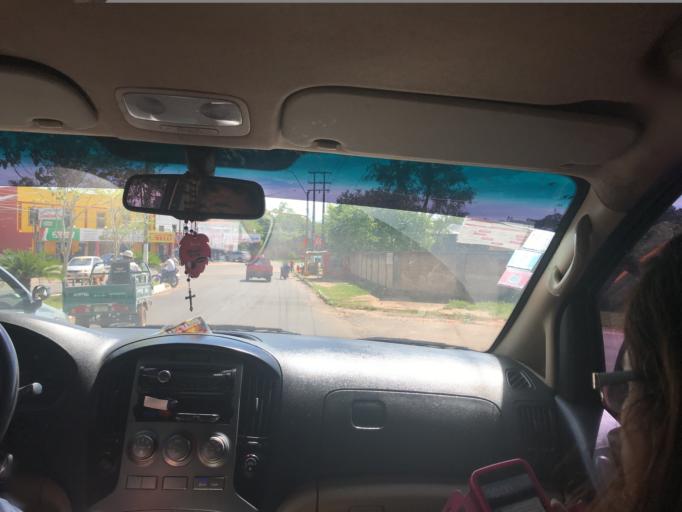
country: PY
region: San Pedro
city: Guayaybi
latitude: -24.6641
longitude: -56.4364
